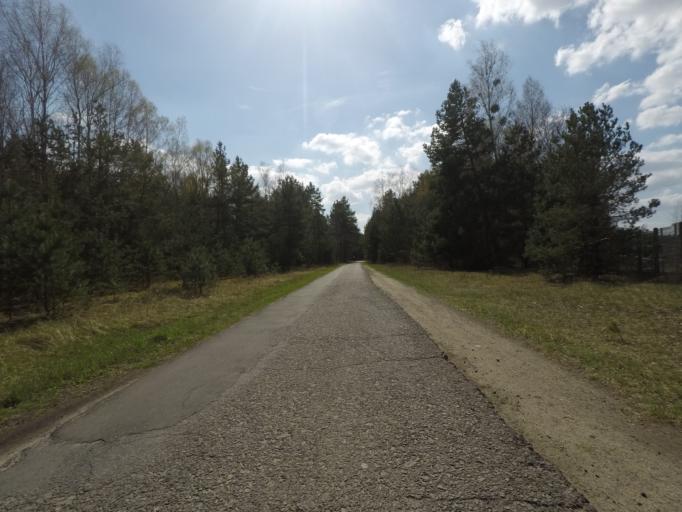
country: DE
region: Brandenburg
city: Melchow
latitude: 52.8203
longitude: 13.7126
